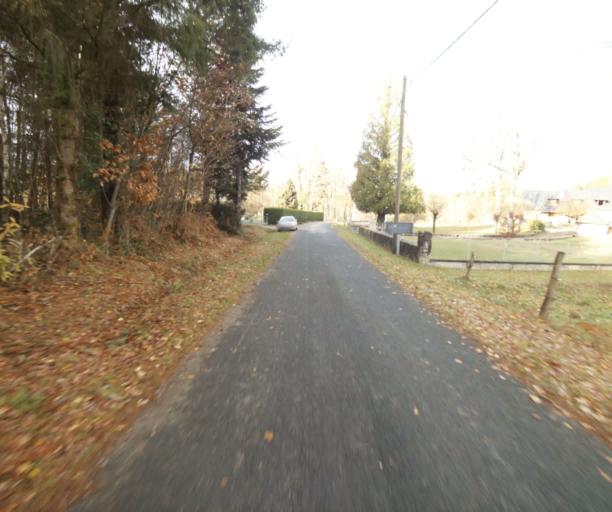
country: FR
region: Limousin
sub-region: Departement de la Correze
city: Sainte-Fortunade
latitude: 45.1945
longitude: 1.7367
